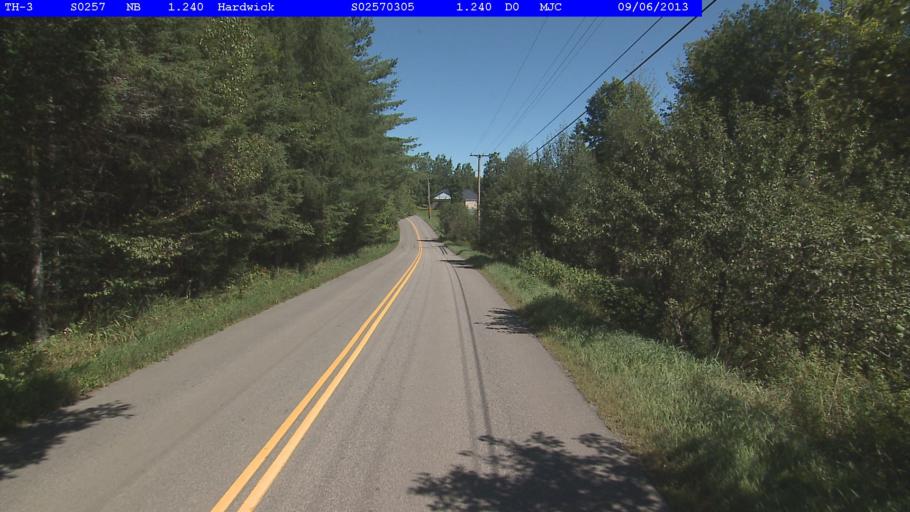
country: US
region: Vermont
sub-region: Caledonia County
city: Hardwick
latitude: 44.5096
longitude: -72.3449
